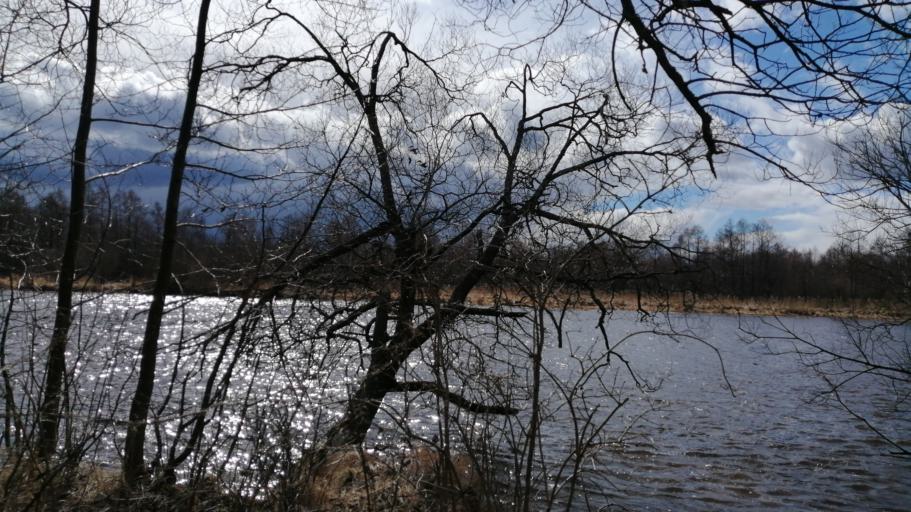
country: EE
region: Tartu
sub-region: Alatskivi vald
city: Kallaste
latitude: 58.3837
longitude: 27.1174
